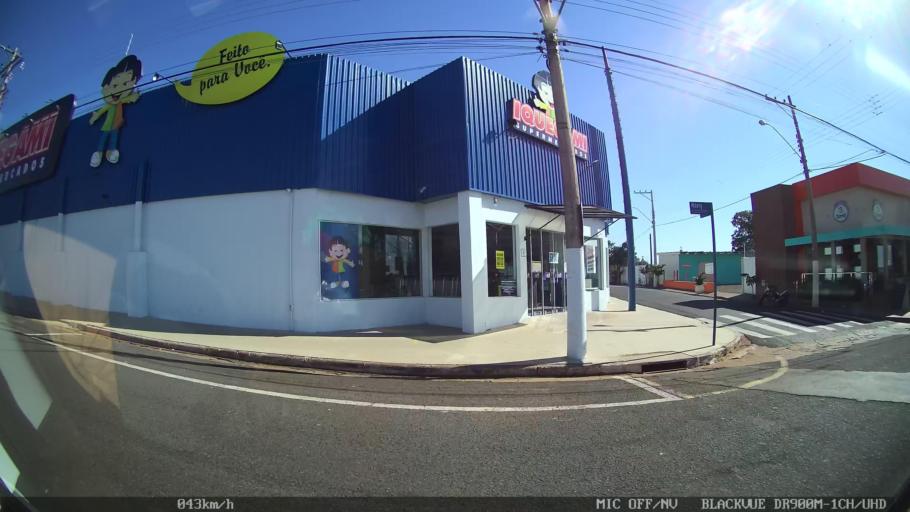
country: BR
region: Sao Paulo
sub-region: Olimpia
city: Olimpia
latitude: -20.7496
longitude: -48.9136
